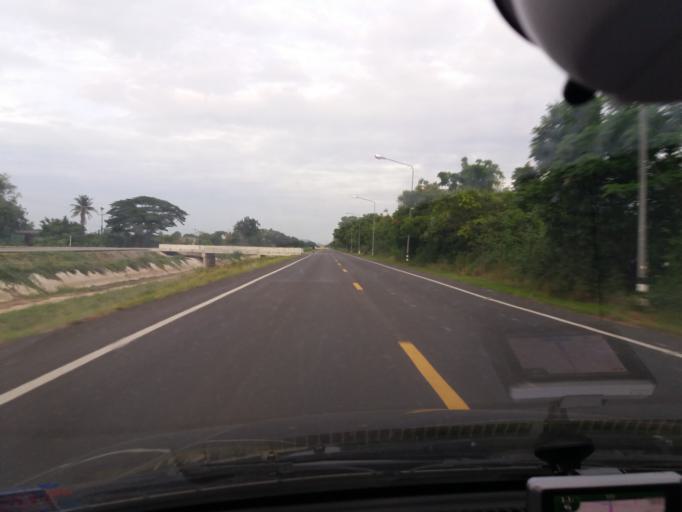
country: TH
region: Suphan Buri
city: U Thong
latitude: 14.5186
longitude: 99.9228
